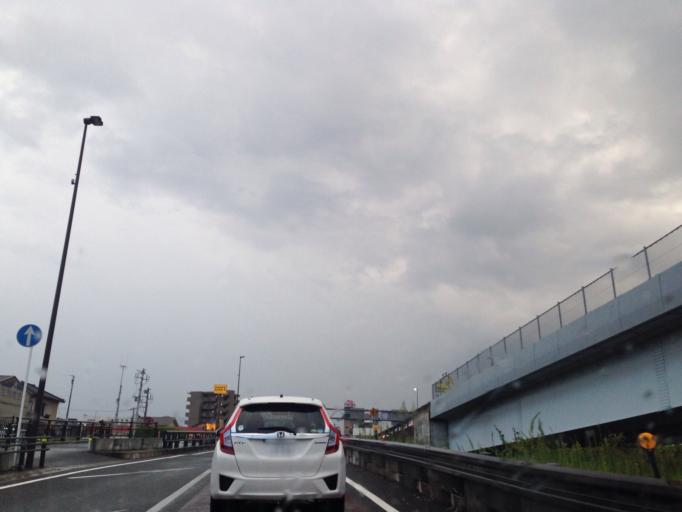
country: JP
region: Shizuoka
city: Mishima
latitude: 35.1115
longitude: 138.9195
